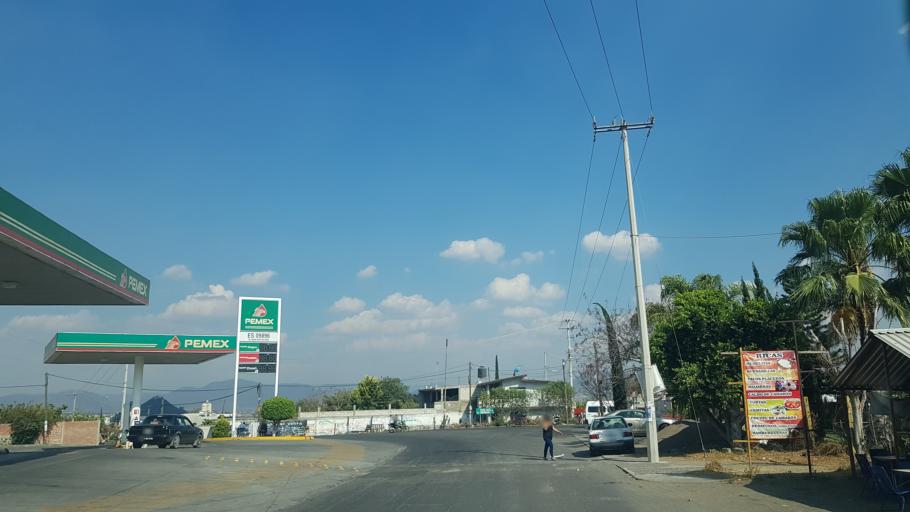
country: MX
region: Puebla
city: Atlixco
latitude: 18.9107
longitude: -98.4743
